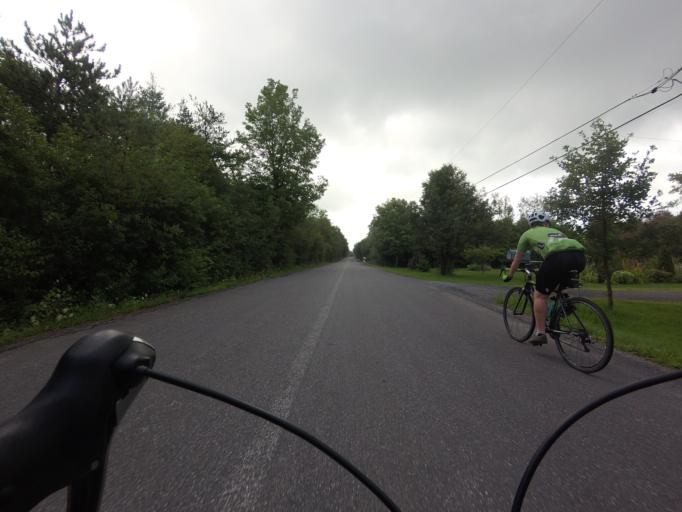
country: CA
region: Ontario
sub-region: Lanark County
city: Smiths Falls
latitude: 44.9536
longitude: -75.7926
